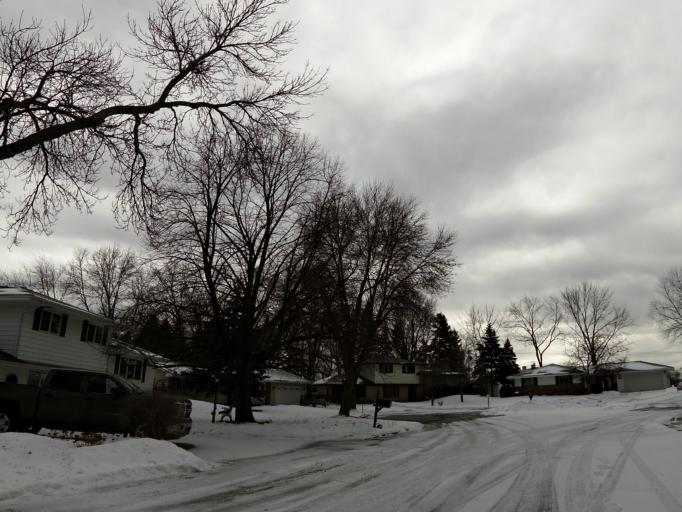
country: US
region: Minnesota
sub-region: Washington County
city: Woodbury
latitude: 44.9285
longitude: -92.9824
